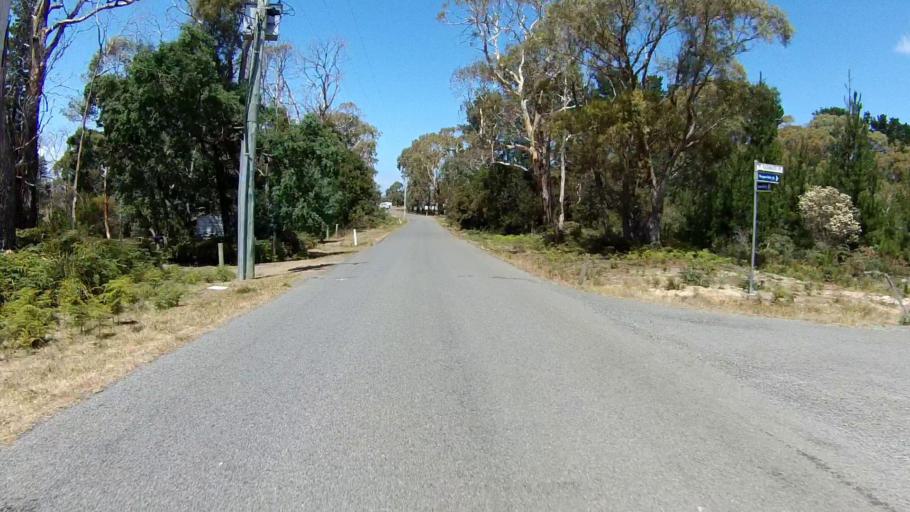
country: AU
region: Tasmania
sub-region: Clarence
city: Sandford
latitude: -42.9322
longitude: 147.4992
